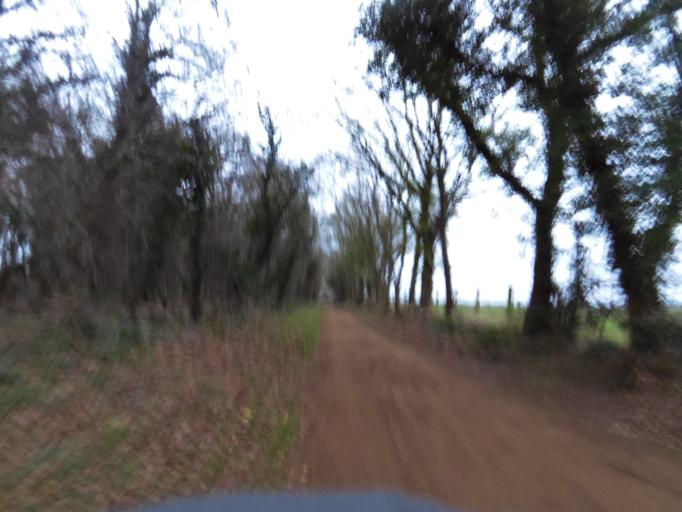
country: GB
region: England
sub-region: Norfolk
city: Costessey
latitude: 52.7048
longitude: 1.1891
